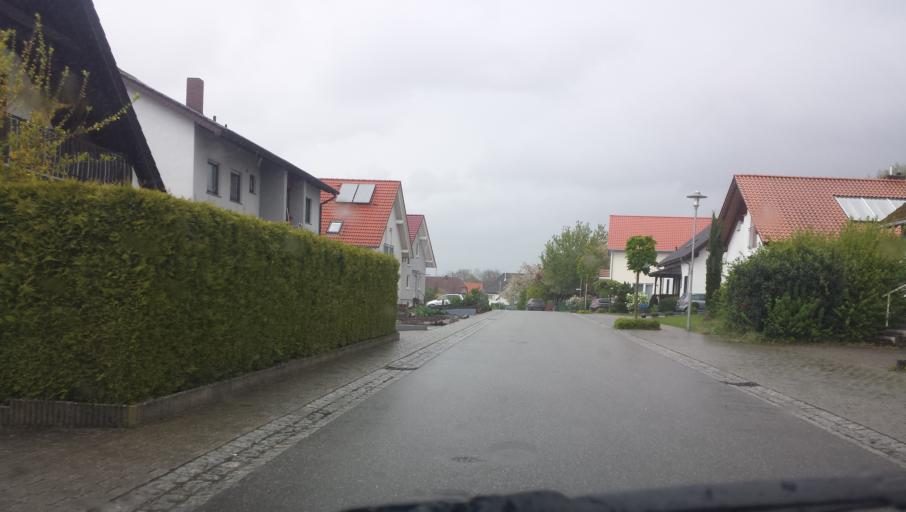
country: DE
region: Rheinland-Pfalz
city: Dierbach
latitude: 49.0815
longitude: 8.0644
